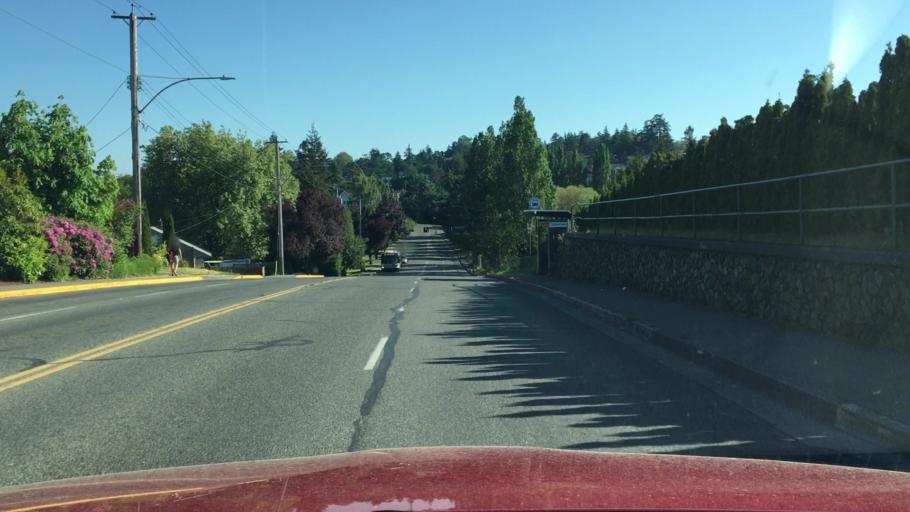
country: CA
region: British Columbia
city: Victoria
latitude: 48.4416
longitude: -123.4023
